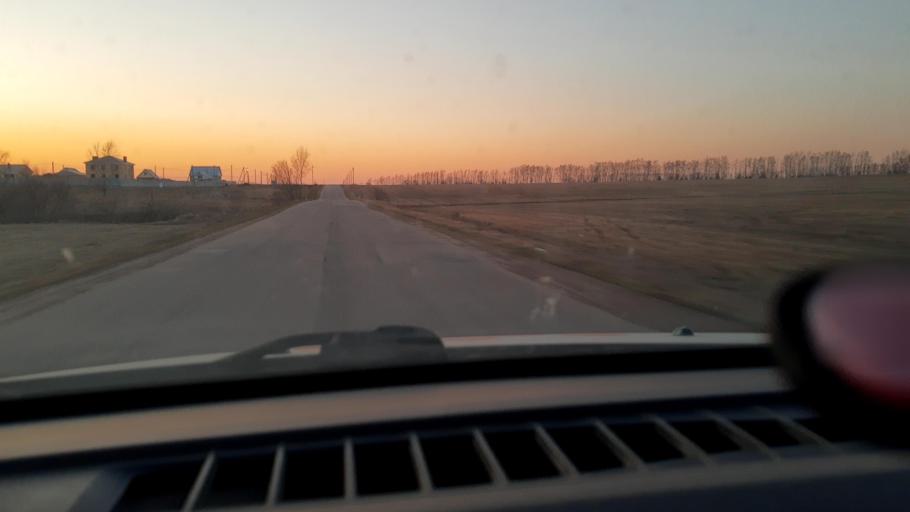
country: RU
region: Bashkortostan
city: Asanovo
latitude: 54.8307
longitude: 55.4637
